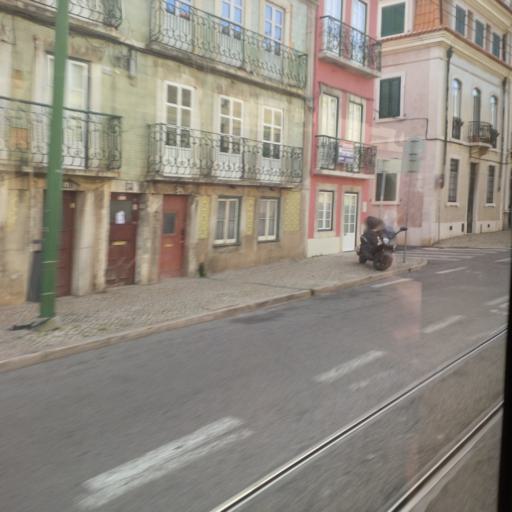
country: PT
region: Setubal
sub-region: Almada
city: Caparica
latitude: 38.6976
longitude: -9.1928
